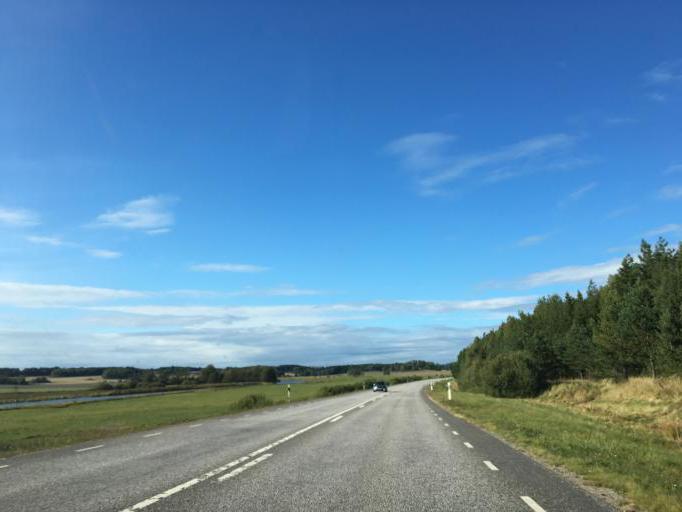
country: SE
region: Soedermanland
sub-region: Nykopings Kommun
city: Nykoping
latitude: 58.7880
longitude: 16.9590
